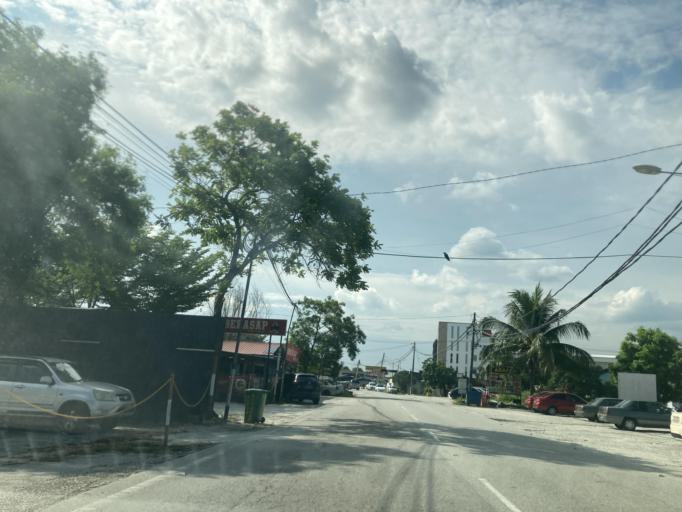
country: MY
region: Selangor
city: Kampung Baru Subang
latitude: 3.1406
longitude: 101.5467
